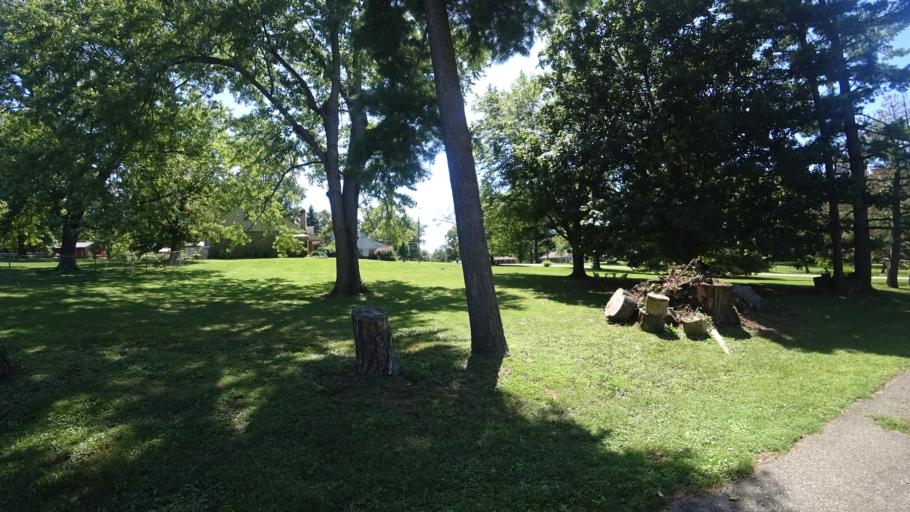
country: US
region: Ohio
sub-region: Butler County
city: New Miami
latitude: 39.4086
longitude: -84.5261
